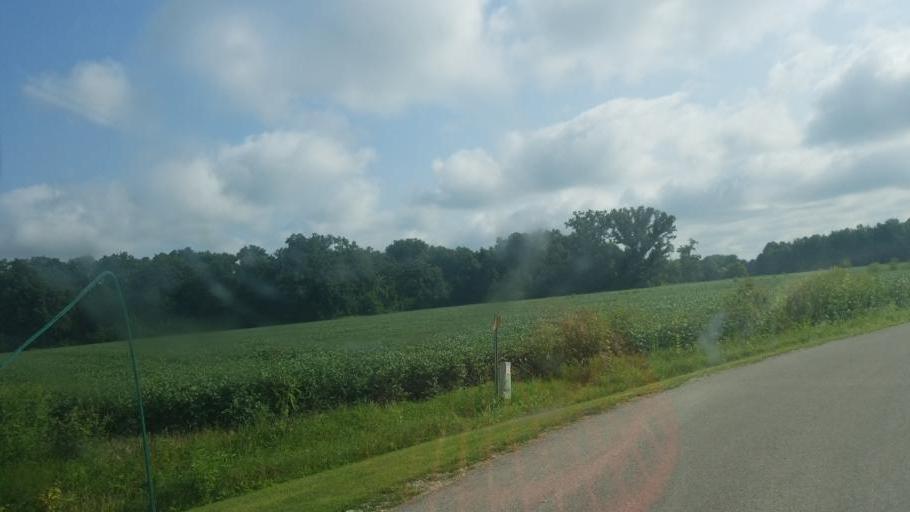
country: US
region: Ohio
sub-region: Marion County
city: Marion
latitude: 40.5755
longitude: -83.0053
